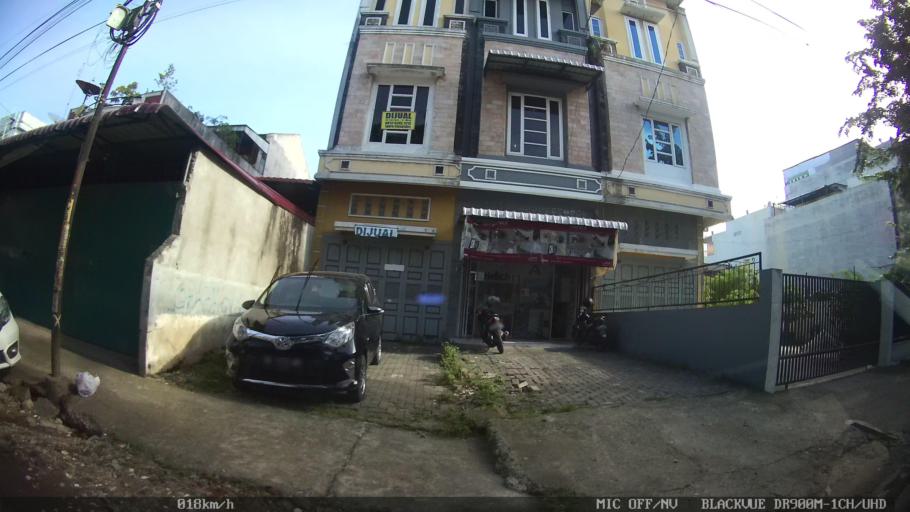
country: ID
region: North Sumatra
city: Medan
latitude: 3.6041
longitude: 98.6570
